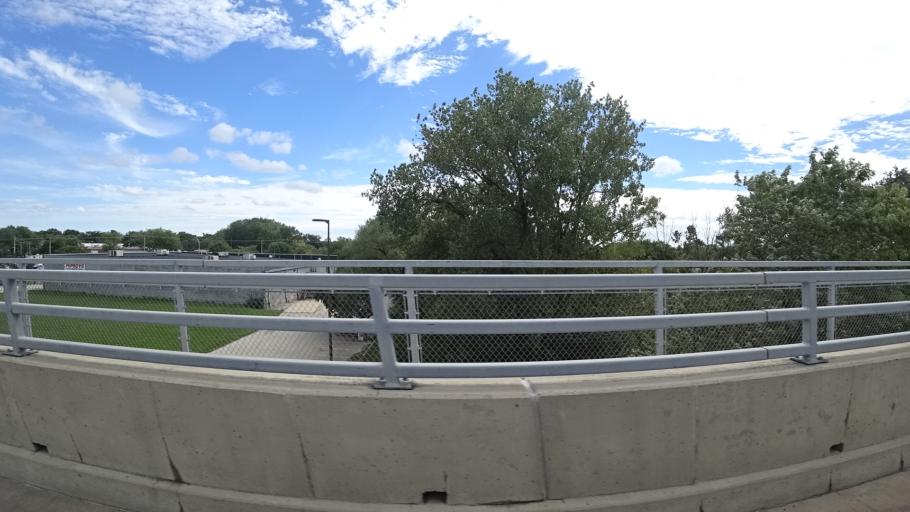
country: US
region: Illinois
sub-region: Cook County
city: Chicago Ridge
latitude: 41.7082
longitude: -87.7814
